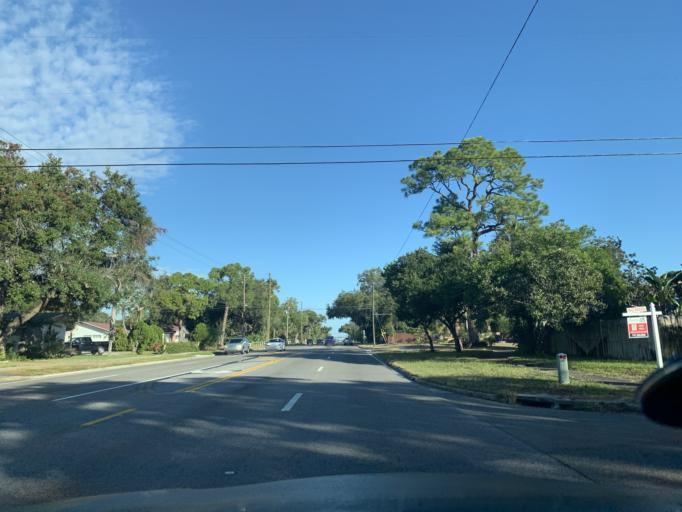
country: US
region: Florida
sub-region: Pinellas County
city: Bay Pines
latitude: 27.8026
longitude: -82.7537
